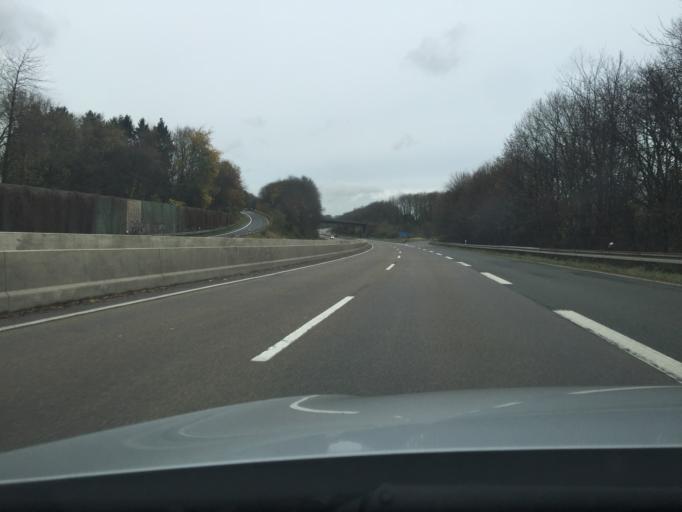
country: DE
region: North Rhine-Westphalia
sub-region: Regierungsbezirk Dusseldorf
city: Velbert
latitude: 51.3152
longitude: 7.0725
